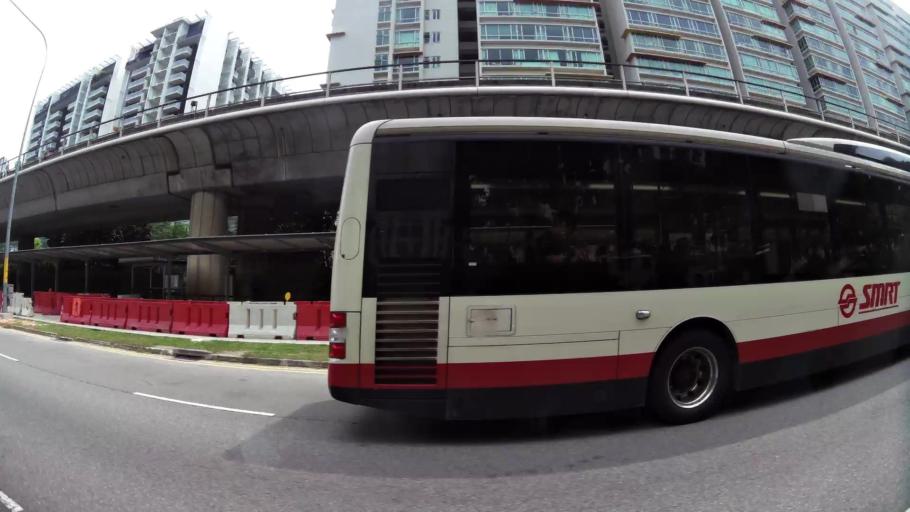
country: MY
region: Johor
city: Johor Bahru
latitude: 1.3435
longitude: 103.7181
